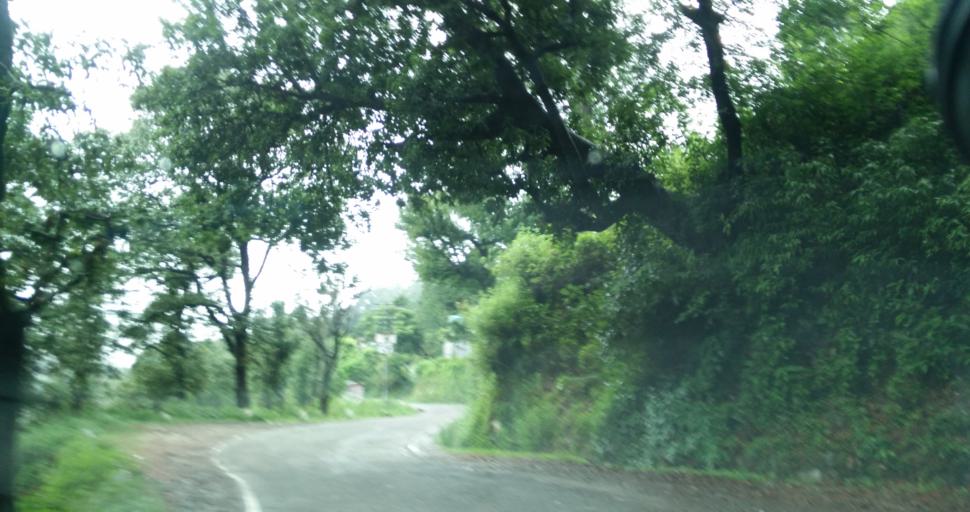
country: IN
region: Uttarakhand
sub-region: Garhwal
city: Lansdowne
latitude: 29.8613
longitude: 78.6813
